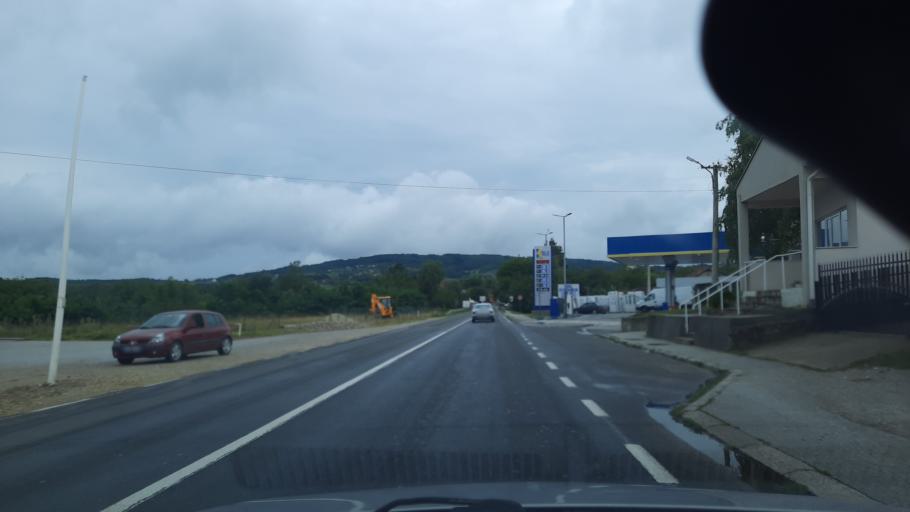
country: RS
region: Central Serbia
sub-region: Sumadijski Okrug
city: Kragujevac
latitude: 43.9764
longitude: 20.8238
